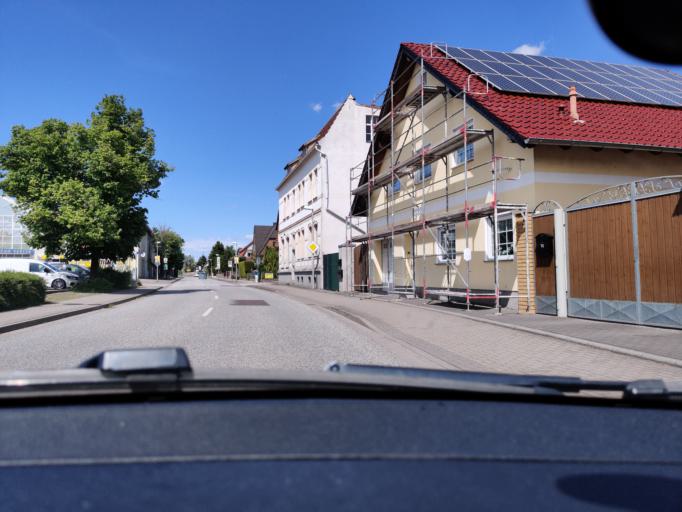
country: DE
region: Saxony-Anhalt
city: Gommern
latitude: 52.0743
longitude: 11.8297
